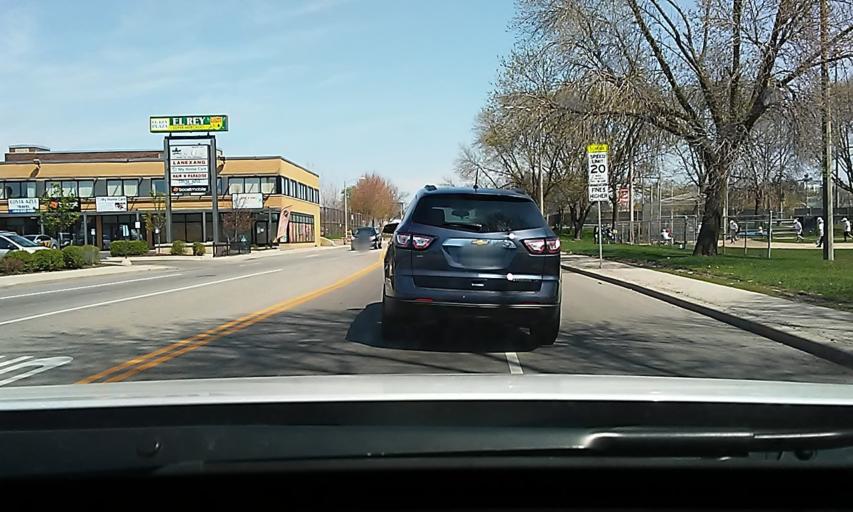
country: US
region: Wisconsin
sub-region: Milwaukee County
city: West Milwaukee
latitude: 43.0104
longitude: -87.9576
